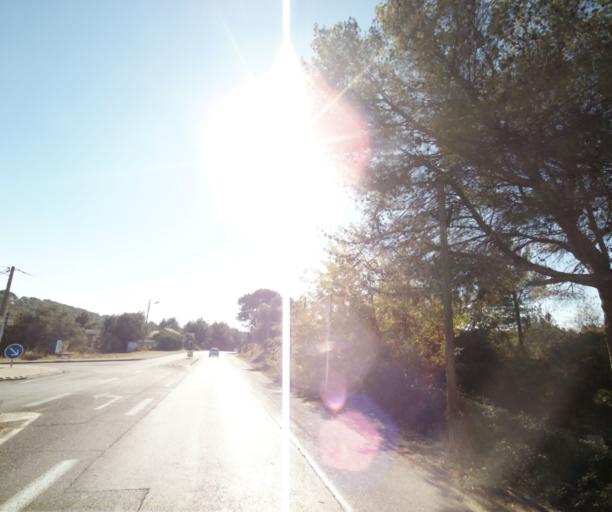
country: FR
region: Provence-Alpes-Cote d'Azur
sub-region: Departement des Bouches-du-Rhone
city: Ceyreste
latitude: 43.2081
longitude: 5.6276
